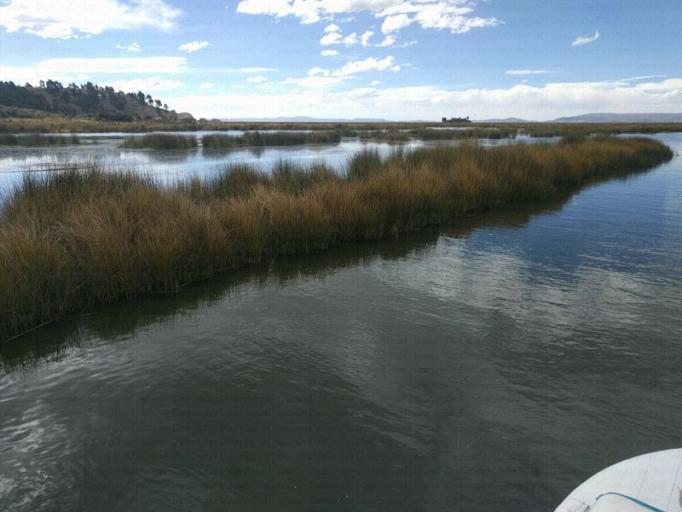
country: PE
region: Puno
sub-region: Provincia de Puno
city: Puno
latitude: -15.8294
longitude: -69.9900
